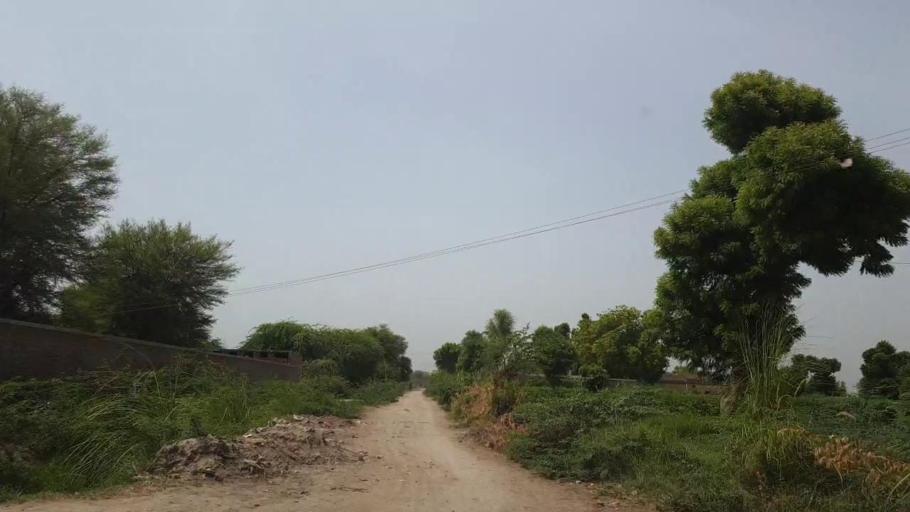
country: PK
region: Sindh
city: Sakrand
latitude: 26.1235
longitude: 68.2865
